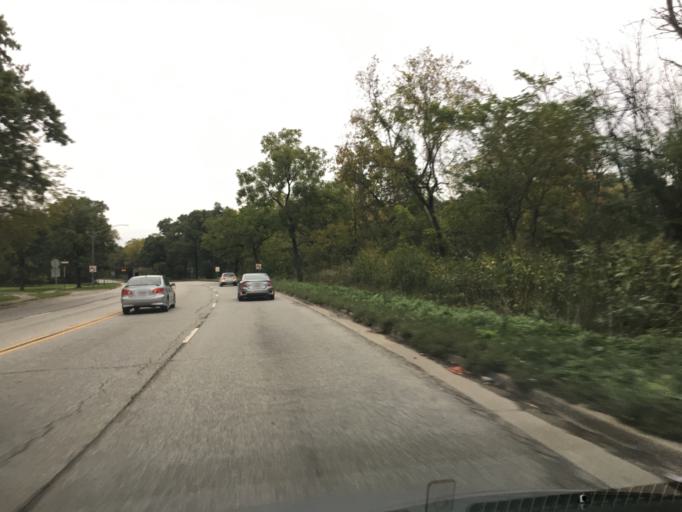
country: US
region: Illinois
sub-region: Cook County
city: Riverside
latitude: 41.8231
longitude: -87.8290
